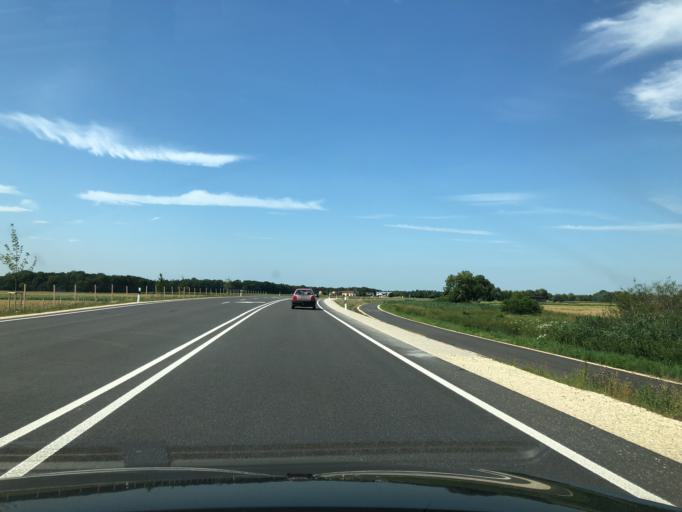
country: DE
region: Bavaria
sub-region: Upper Bavaria
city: Weichering
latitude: 48.7126
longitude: 11.3413
